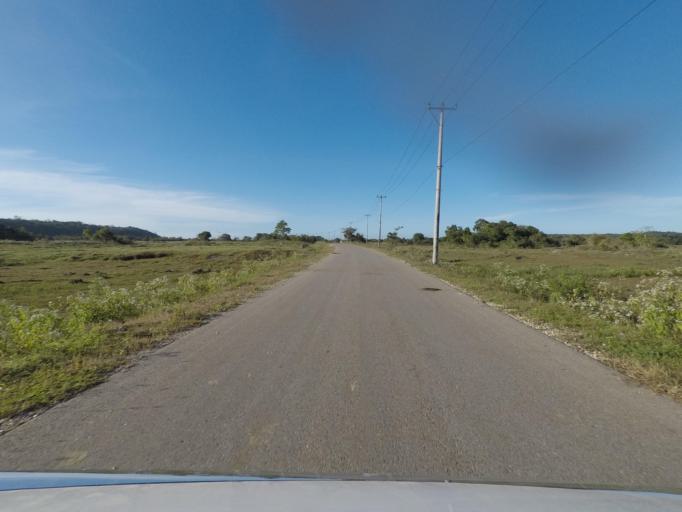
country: TL
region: Lautem
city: Lospalos
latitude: -8.3960
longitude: 127.0080
